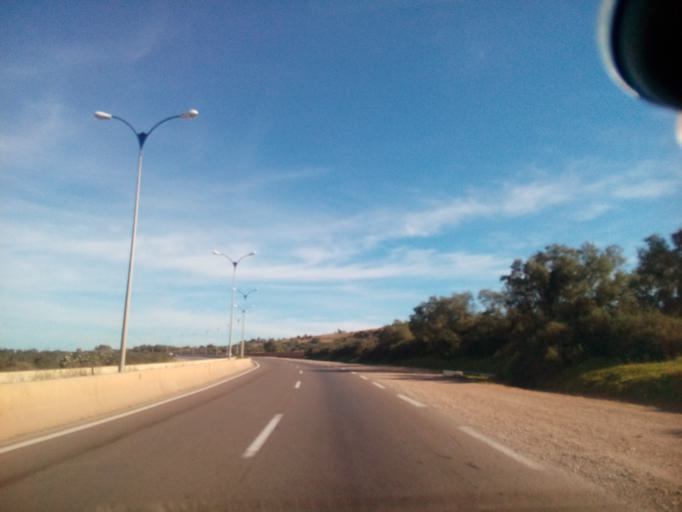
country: DZ
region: Oran
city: Ain el Bya
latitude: 35.7888
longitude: -0.0968
